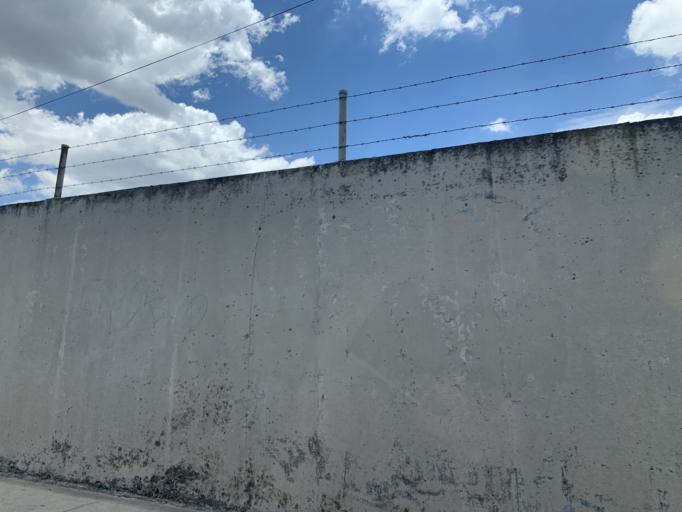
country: MX
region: Puebla
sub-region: Cuautlancingo
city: Sanctorum
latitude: 19.0765
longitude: -98.2391
